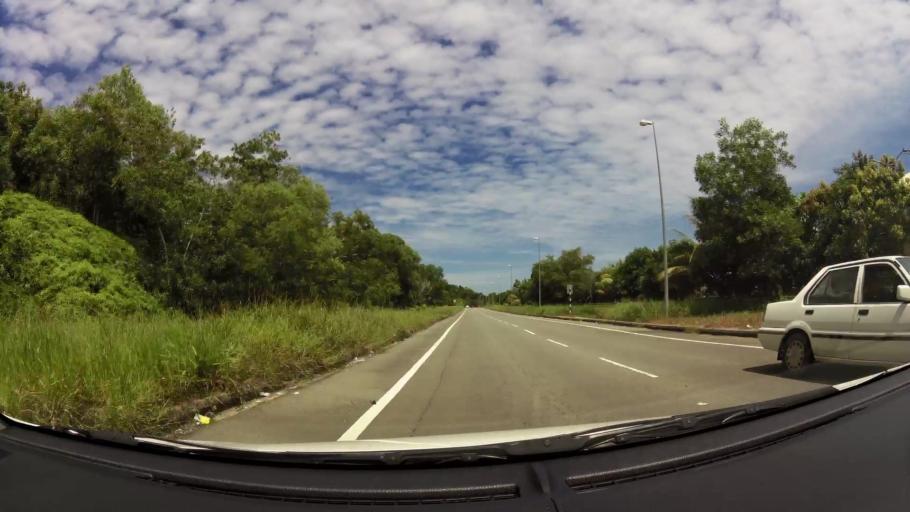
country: BN
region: Brunei and Muara
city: Bandar Seri Begawan
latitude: 4.9919
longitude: 115.0114
